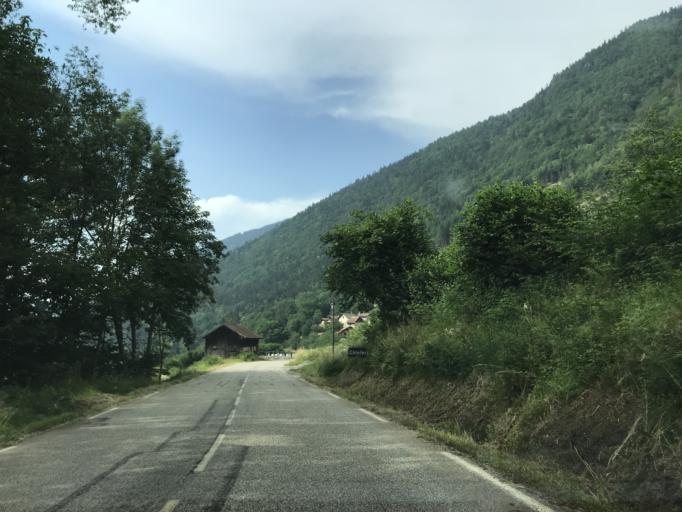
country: FR
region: Rhone-Alpes
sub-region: Departement de l'Isere
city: Allevard
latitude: 45.3661
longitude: 6.0973
